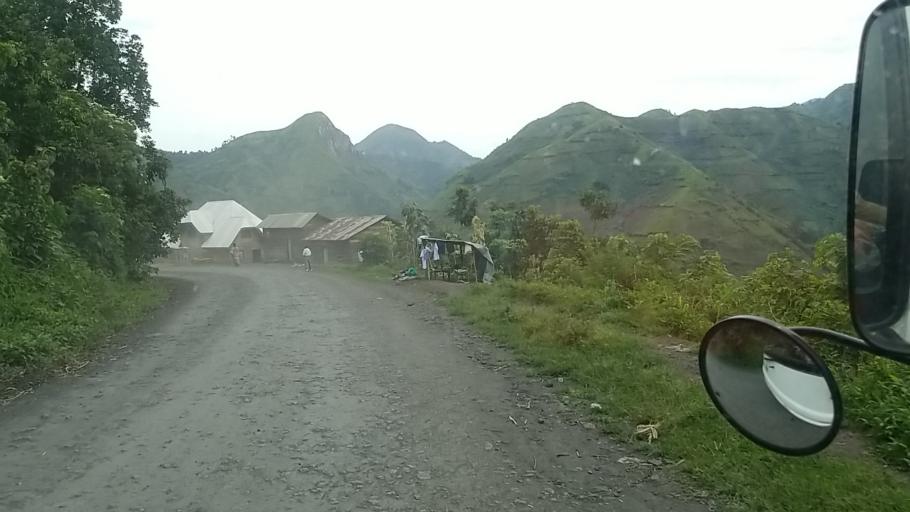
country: CD
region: Nord Kivu
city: Sake
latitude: -1.7594
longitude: 28.9867
